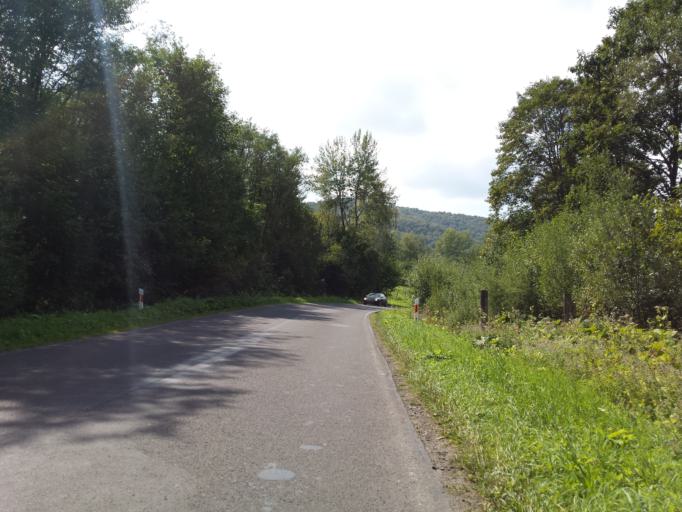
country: PL
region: Subcarpathian Voivodeship
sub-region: Powiat leski
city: Cisna
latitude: 49.1437
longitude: 22.4915
